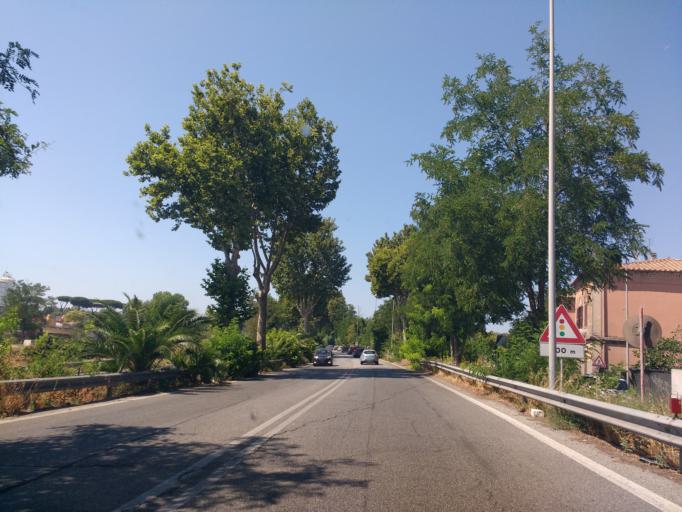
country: IT
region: Latium
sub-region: Citta metropolitana di Roma Capitale
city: Acilia-Castel Fusano-Ostia Antica
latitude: 41.7620
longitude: 12.3064
